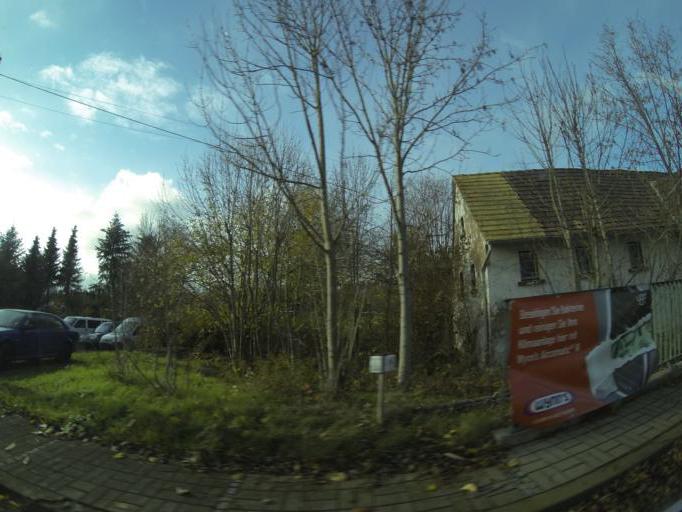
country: DE
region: Thuringia
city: Gossnitz
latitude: 50.9114
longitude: 12.4425
